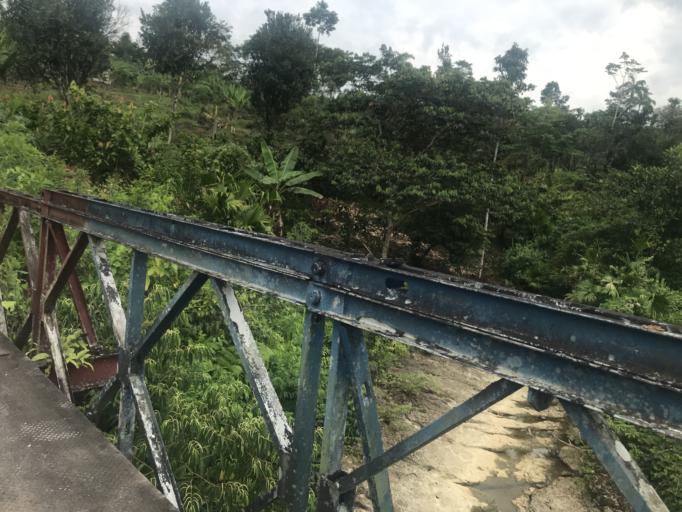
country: EC
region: Napo
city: Tena
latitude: -1.0272
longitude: -77.7423
